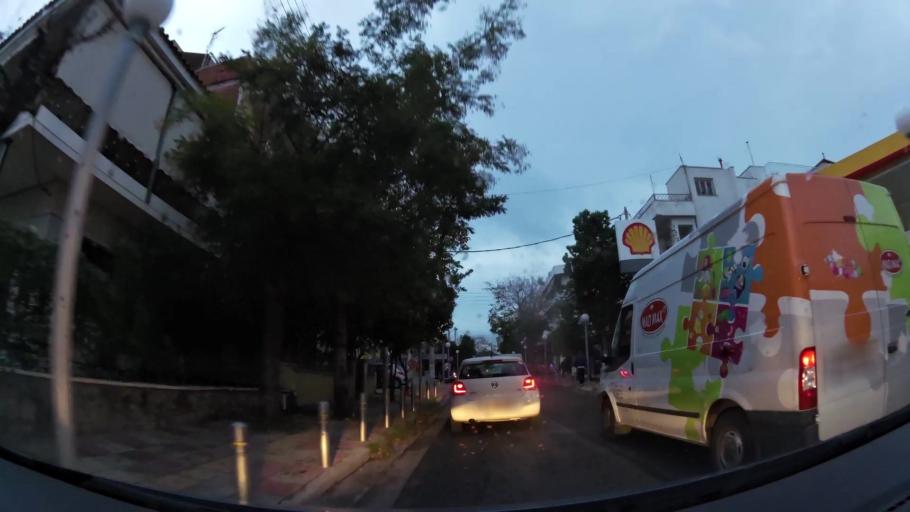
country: GR
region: Attica
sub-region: Nomarchia Athinas
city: Ymittos
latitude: 37.9490
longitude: 23.7428
